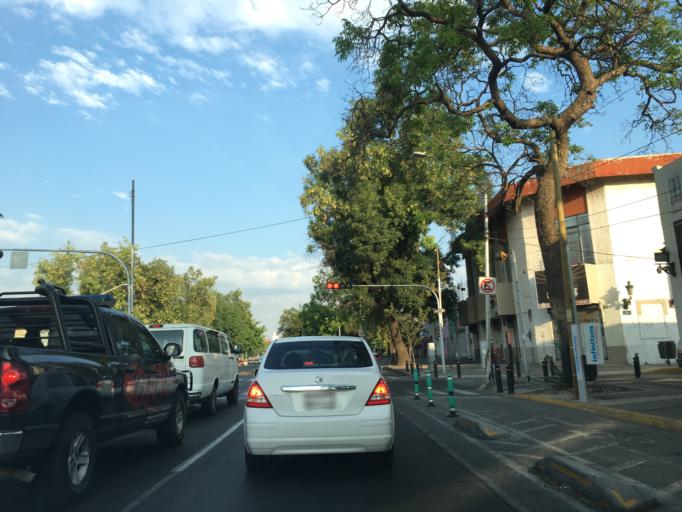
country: MX
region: Jalisco
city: Guadalajara
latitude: 20.6688
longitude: -103.3495
